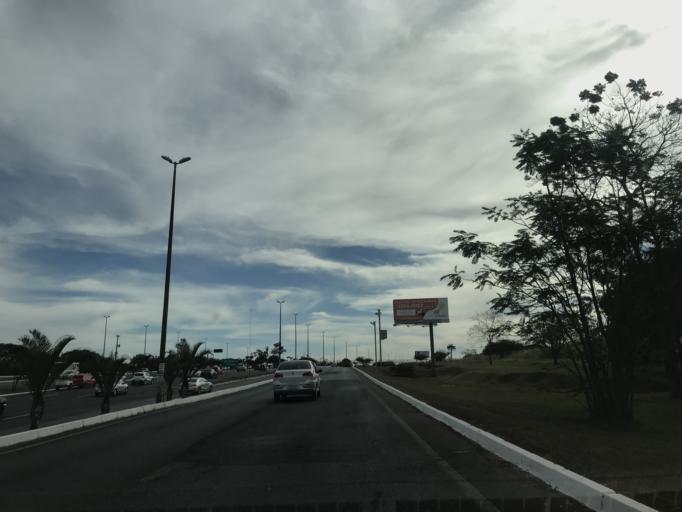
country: BR
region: Federal District
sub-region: Brasilia
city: Brasilia
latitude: -15.8444
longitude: -47.9378
